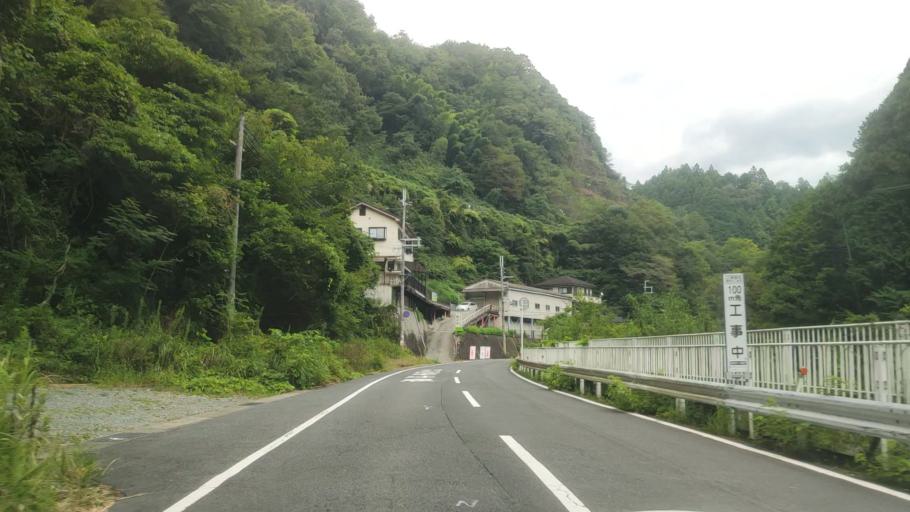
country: JP
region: Wakayama
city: Hashimoto
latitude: 34.2770
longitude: 135.5663
